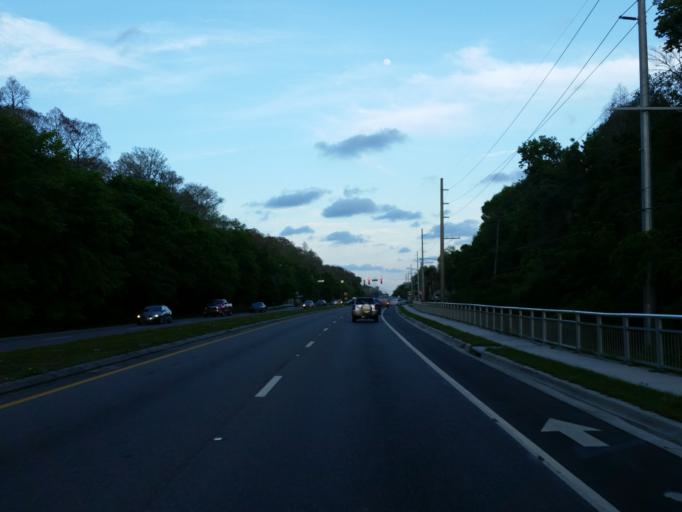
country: US
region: Florida
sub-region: Hillsborough County
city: University
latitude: 28.0691
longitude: -82.4039
